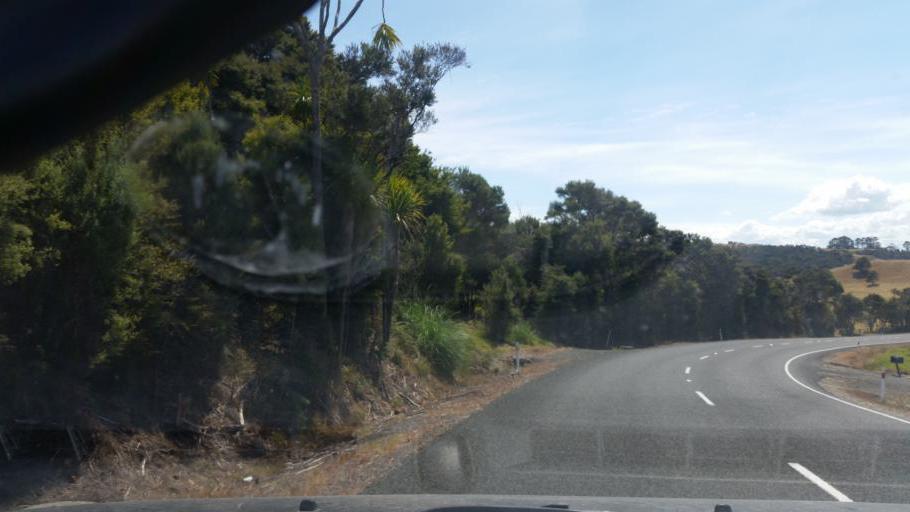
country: NZ
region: Auckland
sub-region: Auckland
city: Wellsford
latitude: -36.1854
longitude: 174.1647
